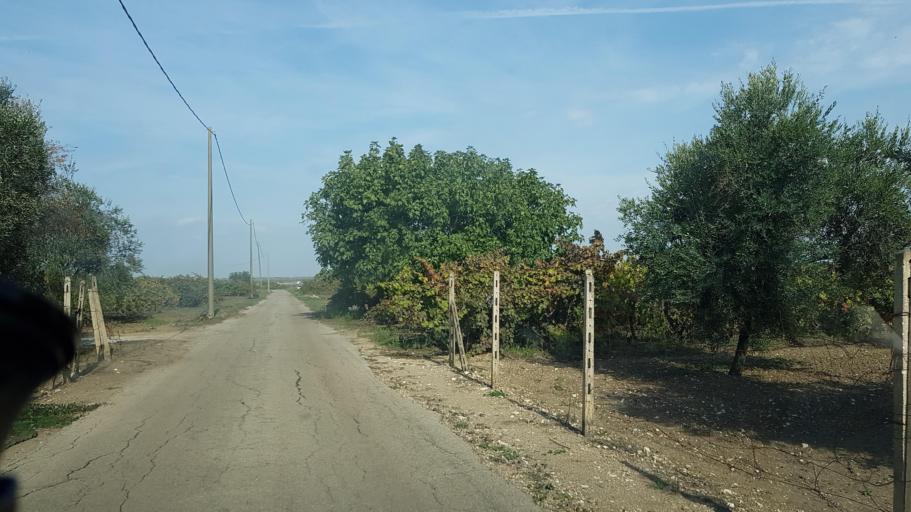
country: IT
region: Apulia
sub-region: Provincia di Brindisi
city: San Pancrazio Salentino
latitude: 40.4294
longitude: 17.8587
